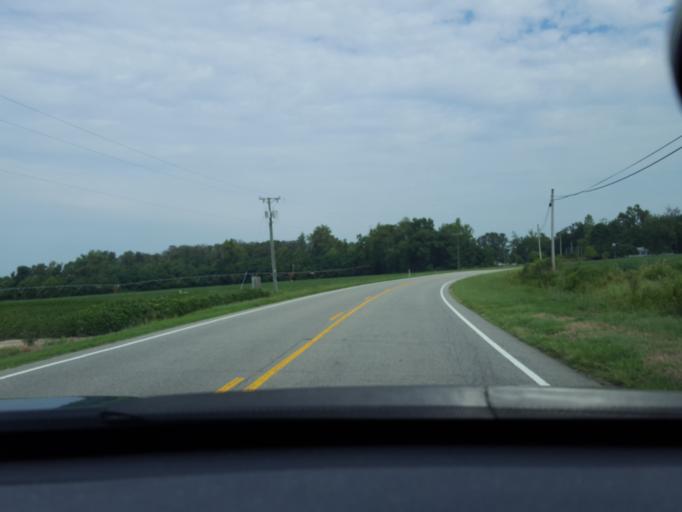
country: US
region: North Carolina
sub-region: Chowan County
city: Edenton
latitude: 36.1990
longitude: -76.6606
